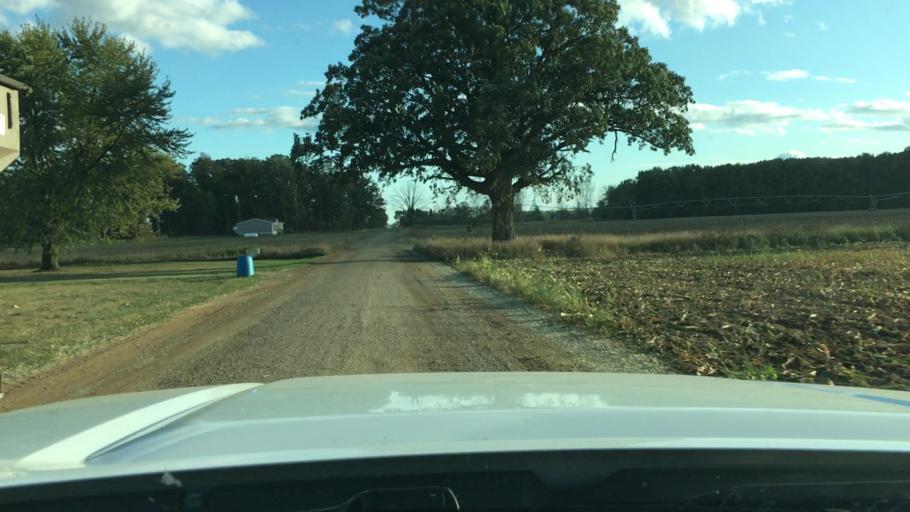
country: US
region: Michigan
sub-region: Clinton County
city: Saint Johns
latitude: 43.0923
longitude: -84.4839
